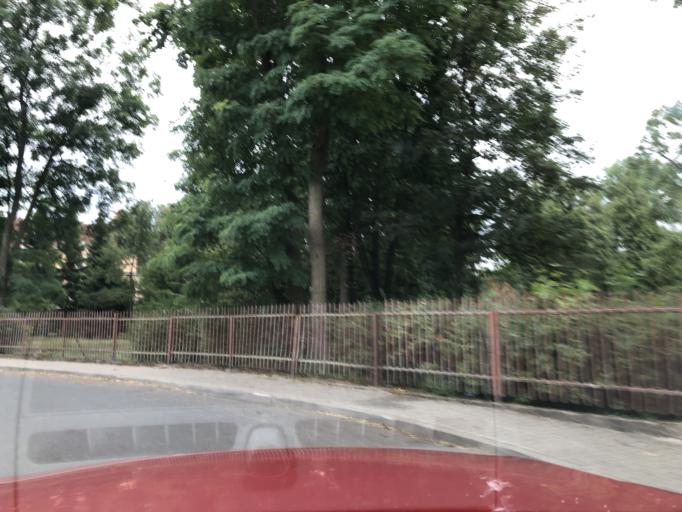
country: PL
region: Greater Poland Voivodeship
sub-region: Powiat szamotulski
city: Pniewy
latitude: 52.5100
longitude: 16.2506
